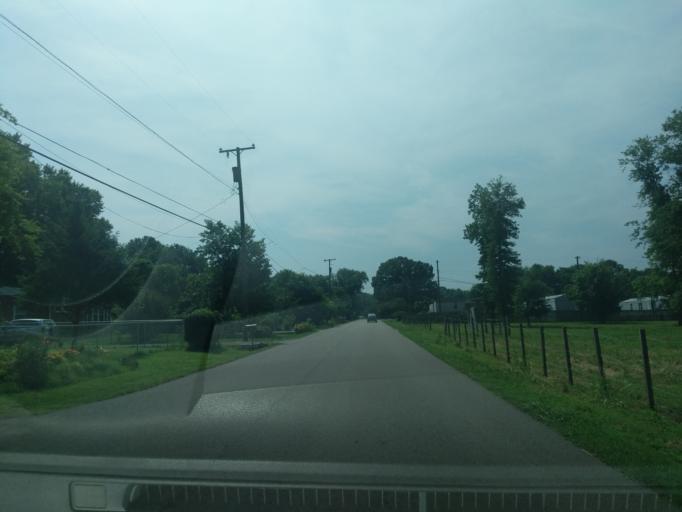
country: US
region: Tennessee
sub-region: Davidson County
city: Lakewood
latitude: 36.2733
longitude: -86.6703
